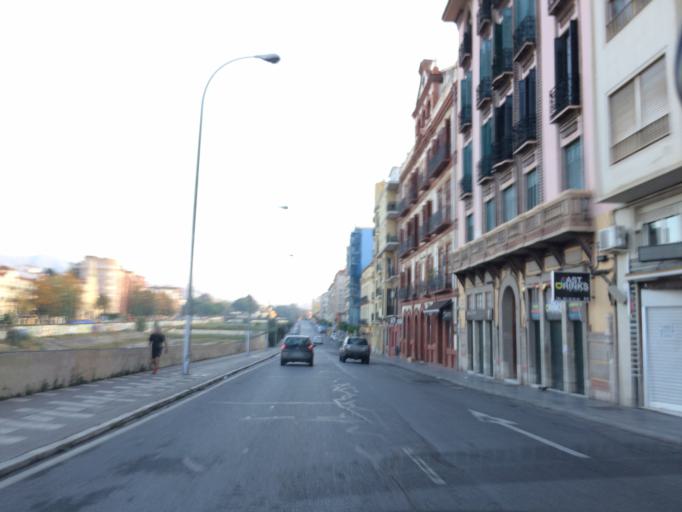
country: ES
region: Andalusia
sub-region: Provincia de Malaga
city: Malaga
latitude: 36.7218
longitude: -4.4253
